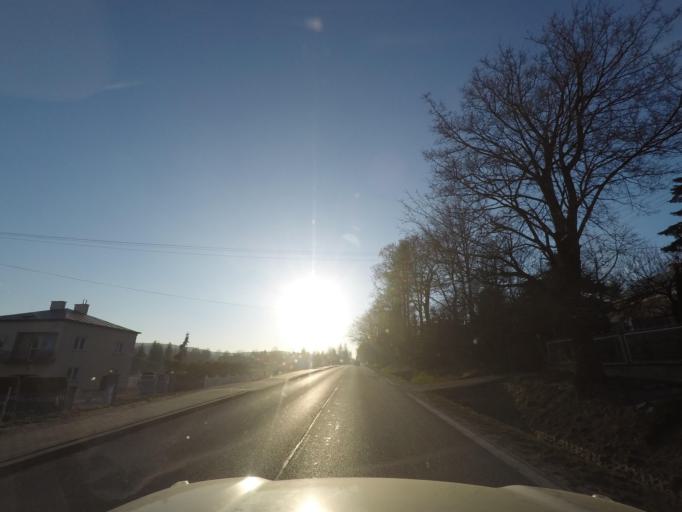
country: PL
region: Subcarpathian Voivodeship
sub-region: Powiat krosnienski
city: Dukla
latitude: 49.5579
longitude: 21.6555
